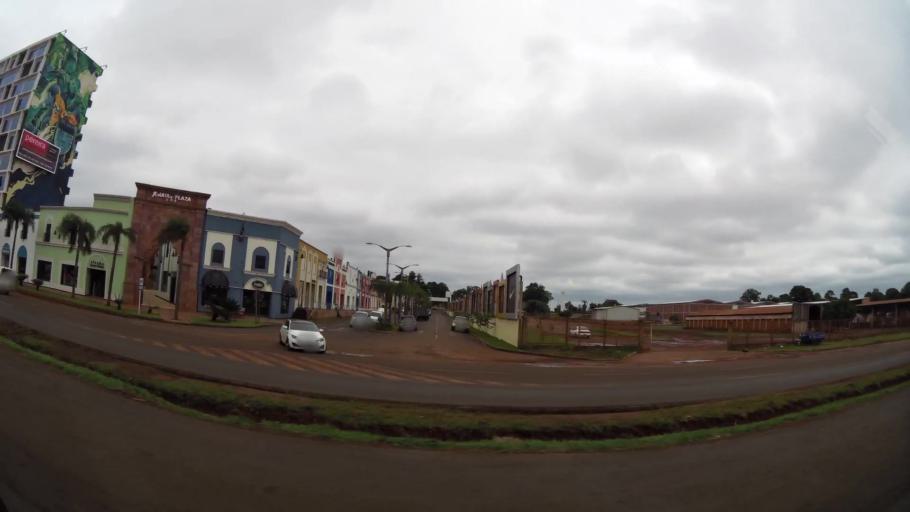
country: PY
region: Alto Parana
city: Ciudad del Este
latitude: -25.4965
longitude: -54.6795
